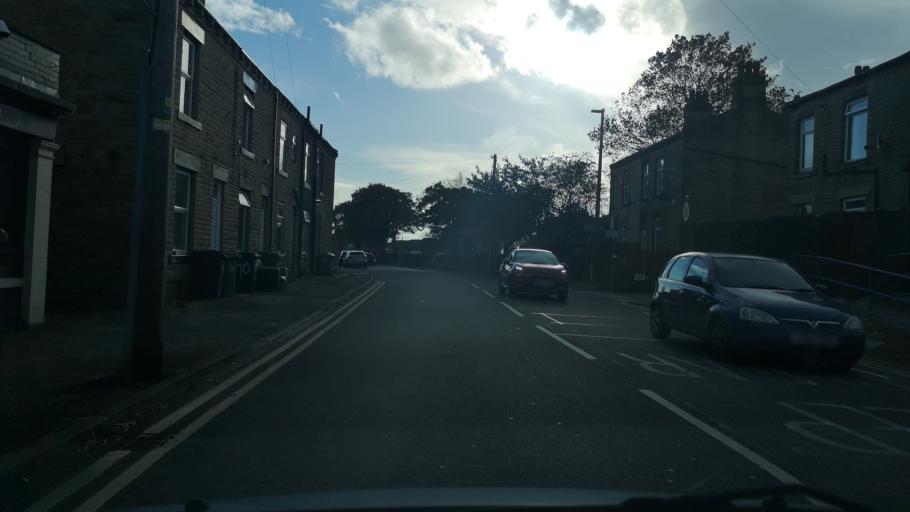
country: GB
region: England
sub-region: Kirklees
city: Batley
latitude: 53.7065
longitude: -1.6542
